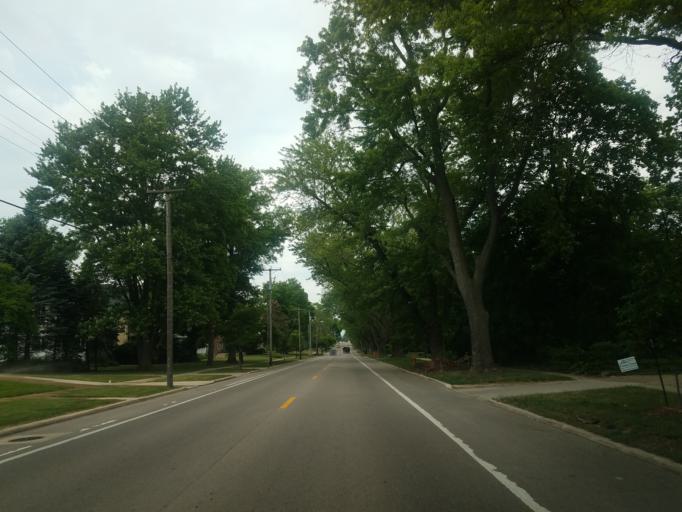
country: US
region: Illinois
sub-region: McLean County
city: Bloomington
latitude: 40.4800
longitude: -88.9686
